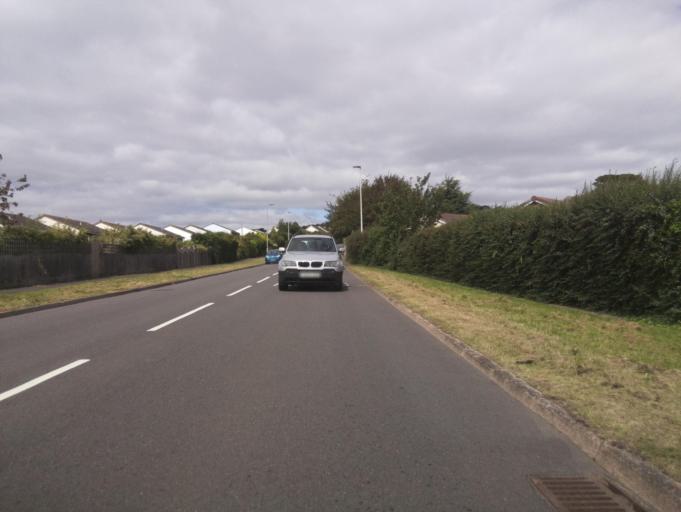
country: GB
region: England
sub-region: Devon
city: Teignmouth
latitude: 50.5558
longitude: -3.5050
